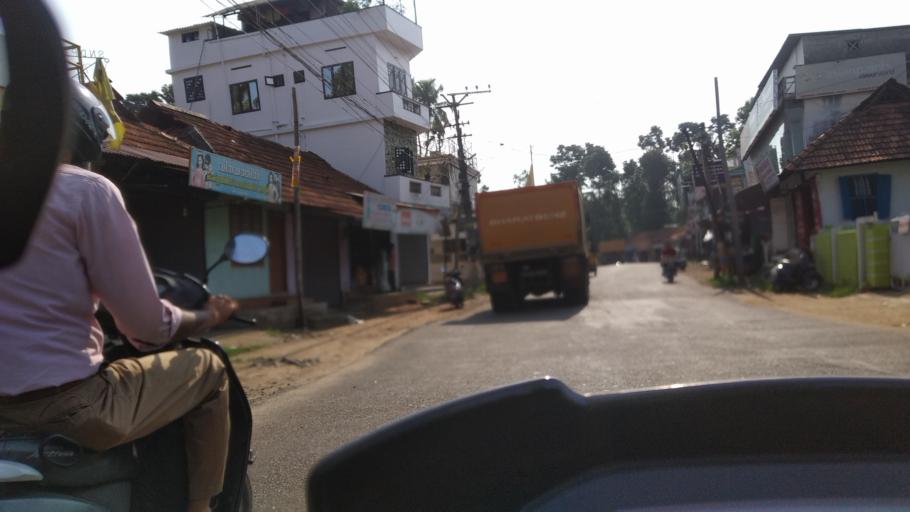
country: IN
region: Kerala
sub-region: Ernakulam
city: Piravam
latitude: 9.8732
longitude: 76.4923
